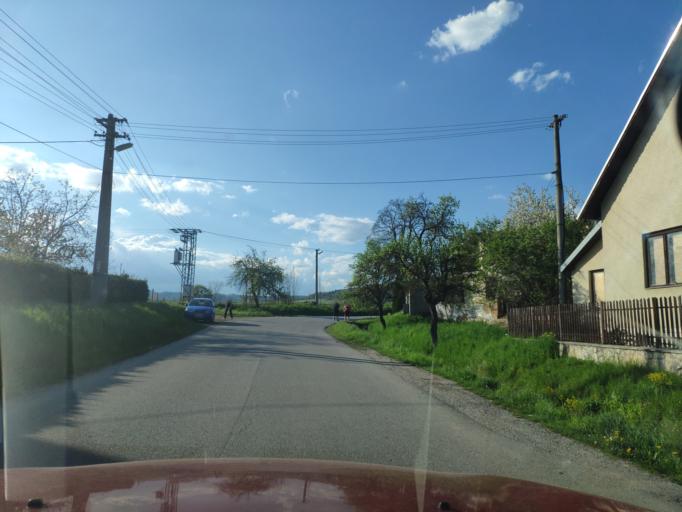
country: SK
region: Presovsky
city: Spisske Podhradie
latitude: 49.0266
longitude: 20.7973
